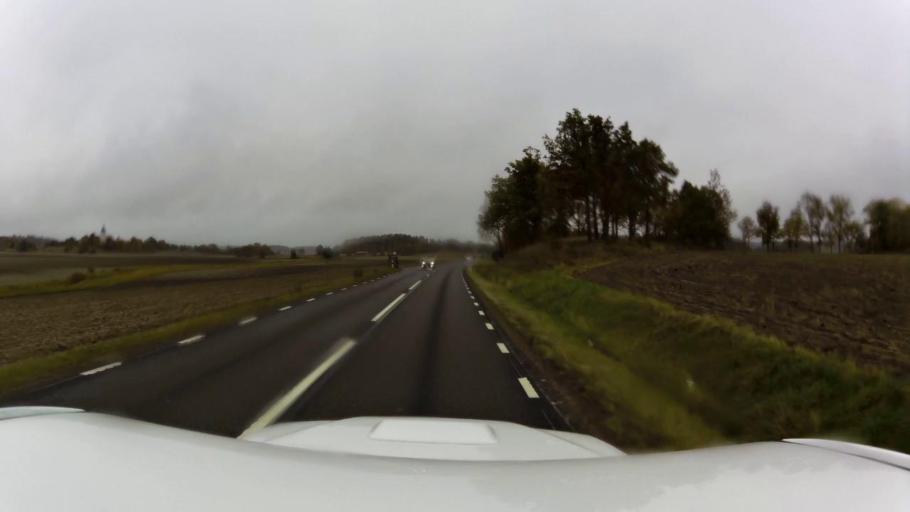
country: SE
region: OEstergoetland
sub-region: Linkopings Kommun
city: Linghem
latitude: 58.3755
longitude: 15.8078
